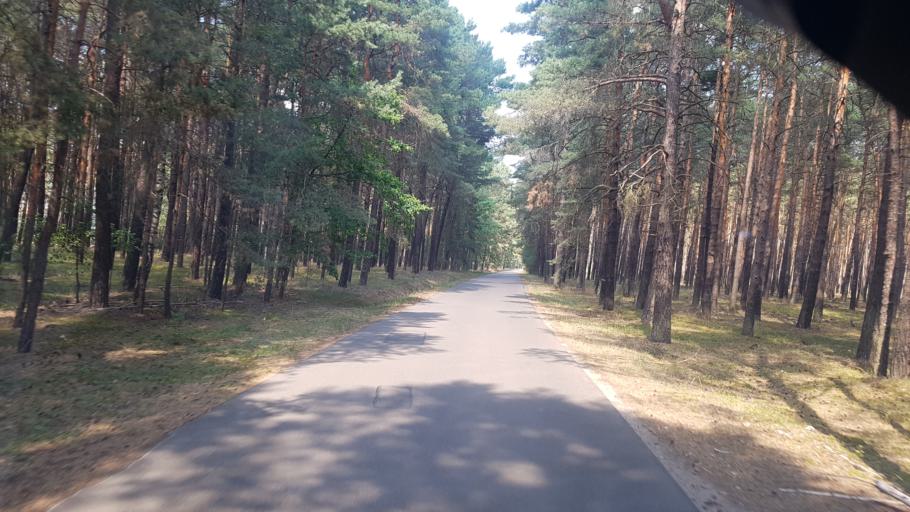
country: DE
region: Brandenburg
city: Spremberg
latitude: 51.6185
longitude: 14.3997
